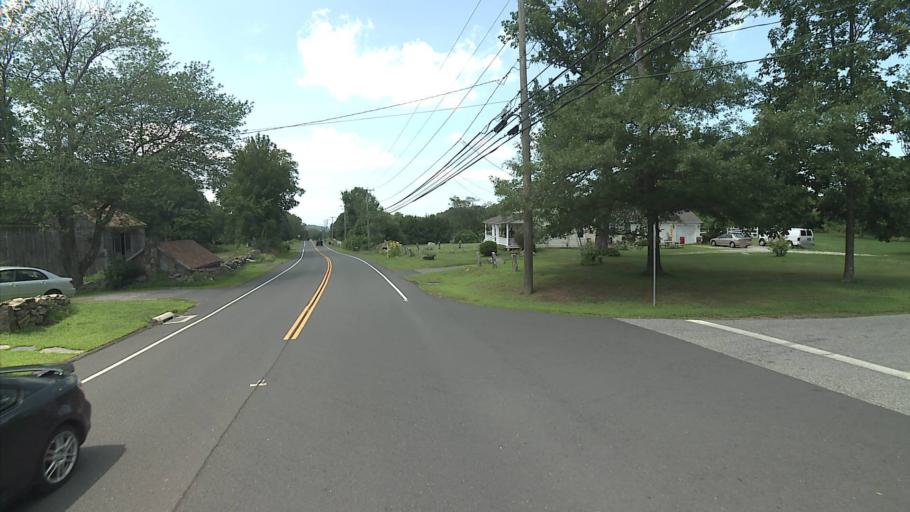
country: US
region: Connecticut
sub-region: Tolland County
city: Rockville
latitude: 41.8429
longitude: -72.4174
